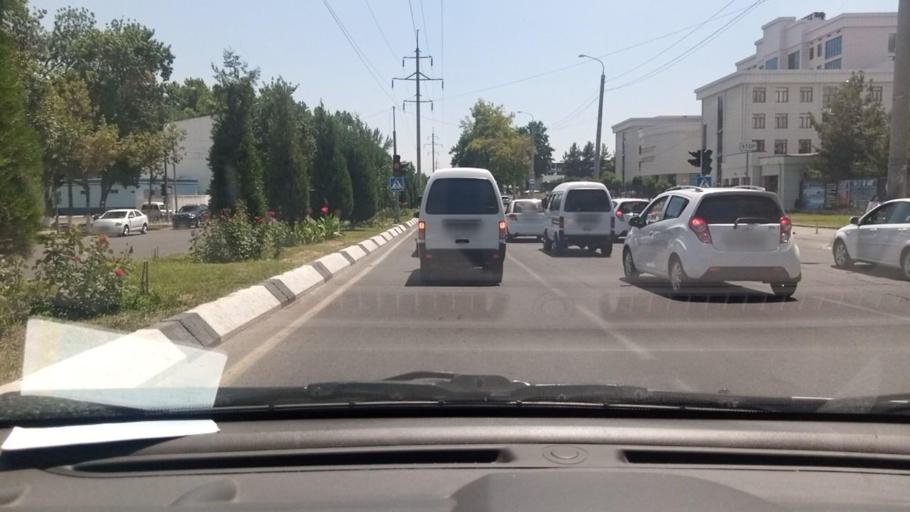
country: UZ
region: Toshkent Shahri
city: Tashkent
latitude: 41.2873
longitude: 69.1944
